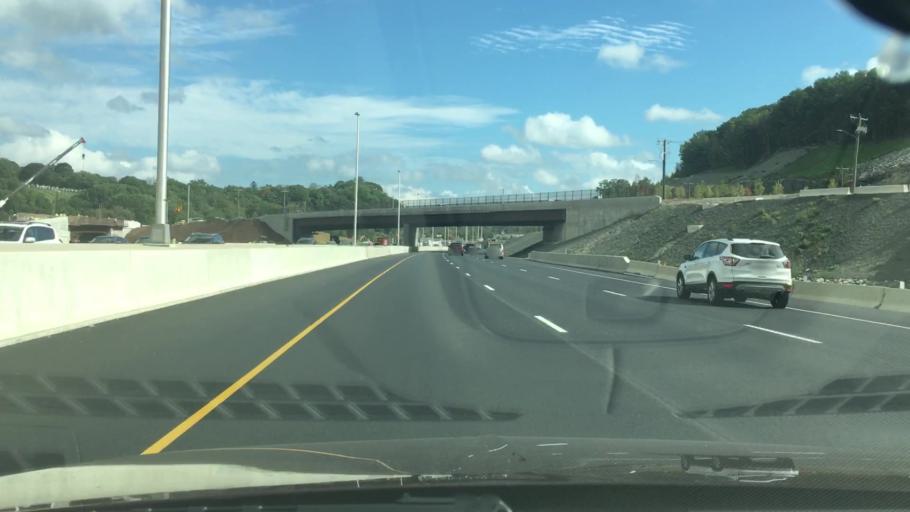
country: US
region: Connecticut
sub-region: New Haven County
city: Waterbury
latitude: 41.5394
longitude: -73.0129
